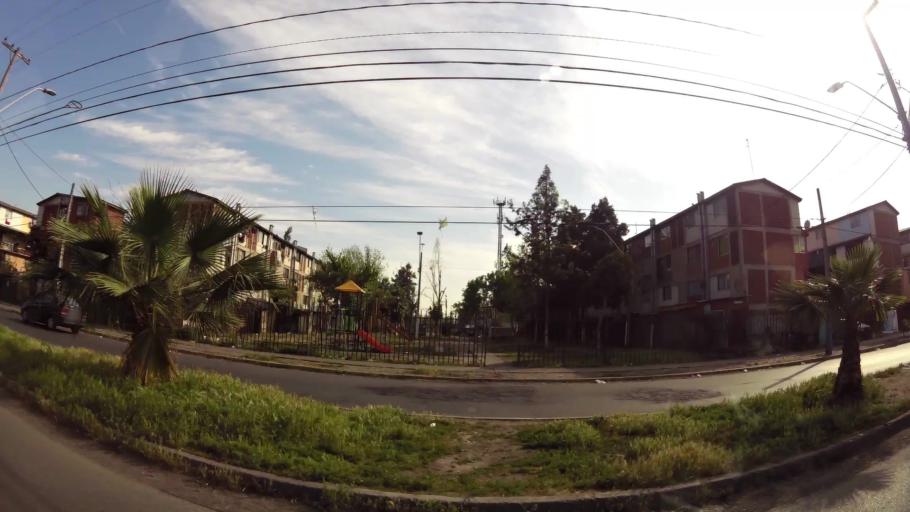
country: CL
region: Santiago Metropolitan
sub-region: Provincia de Santiago
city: La Pintana
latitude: -33.5450
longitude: -70.6358
